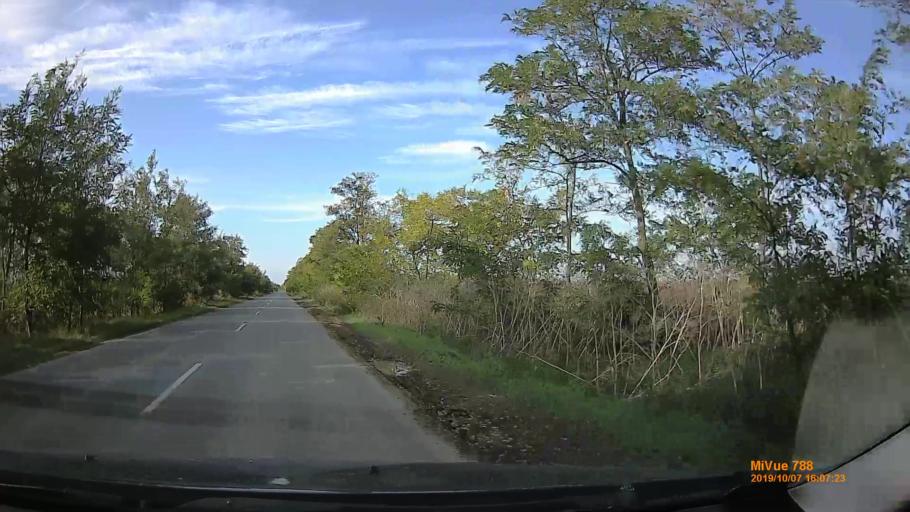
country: HU
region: Bekes
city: Szarvas
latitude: 46.8003
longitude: 20.6209
